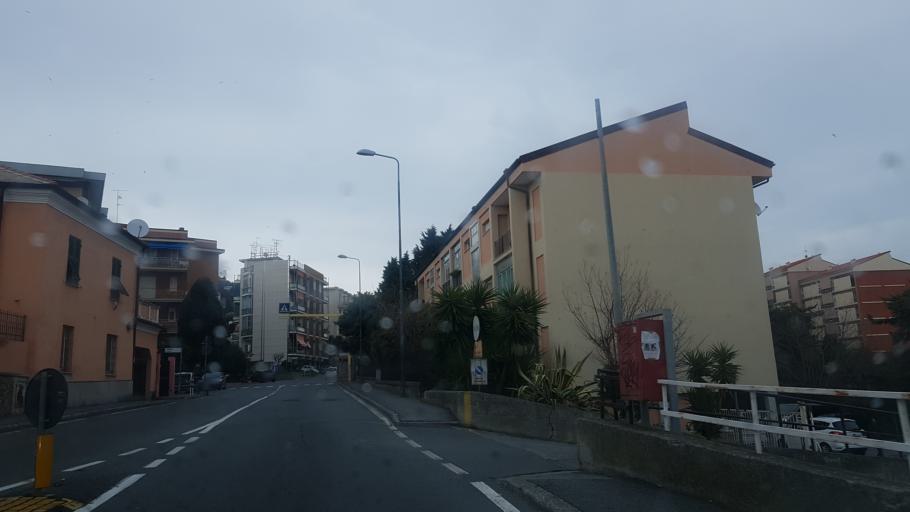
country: IT
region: Liguria
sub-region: Provincia di Savona
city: Savona
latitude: 44.3024
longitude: 8.4592
